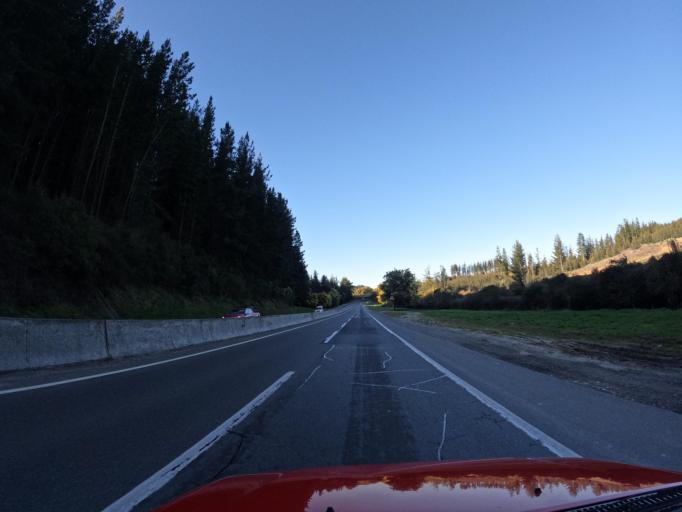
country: CL
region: Biobio
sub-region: Provincia de Concepcion
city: Penco
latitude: -36.7280
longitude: -72.8408
